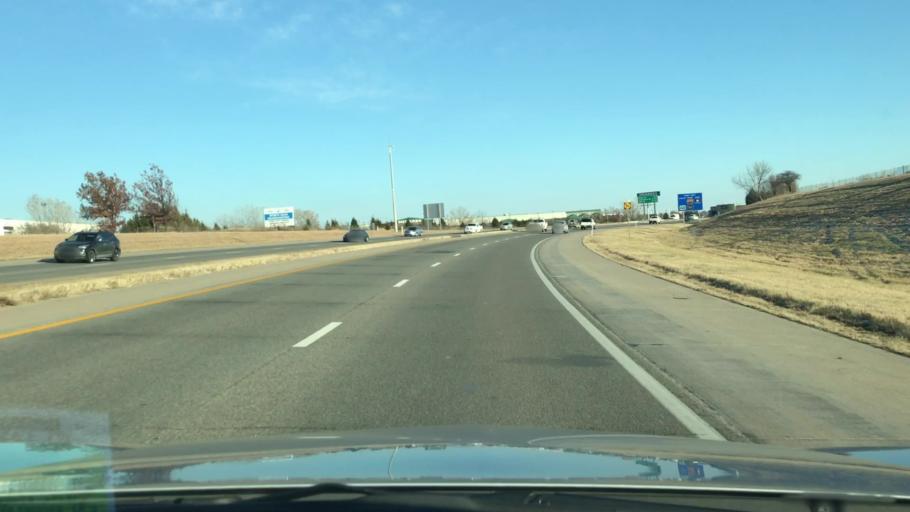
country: US
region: Kansas
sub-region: Sedgwick County
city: Bellaire
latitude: 37.7443
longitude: -97.2368
